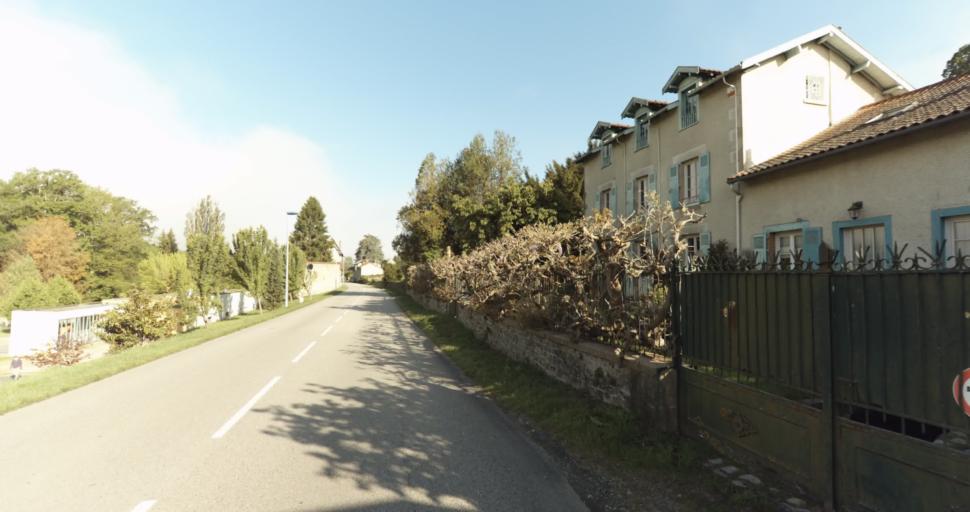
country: FR
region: Limousin
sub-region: Departement de la Haute-Vienne
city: Le Vigen
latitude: 45.7520
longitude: 1.2857
